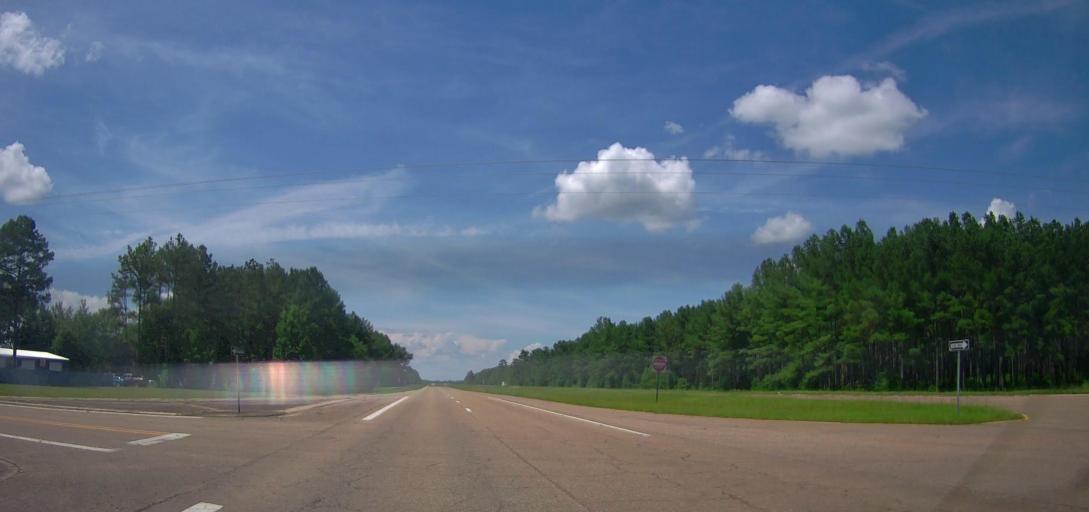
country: US
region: Mississippi
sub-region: Monroe County
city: Aberdeen
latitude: 33.8253
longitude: -88.5849
